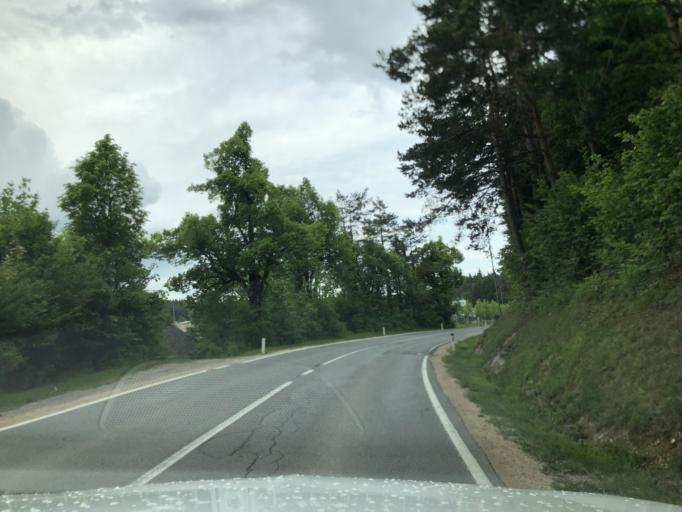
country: SI
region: Cerknica
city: Rakek
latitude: 45.8021
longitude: 14.3297
